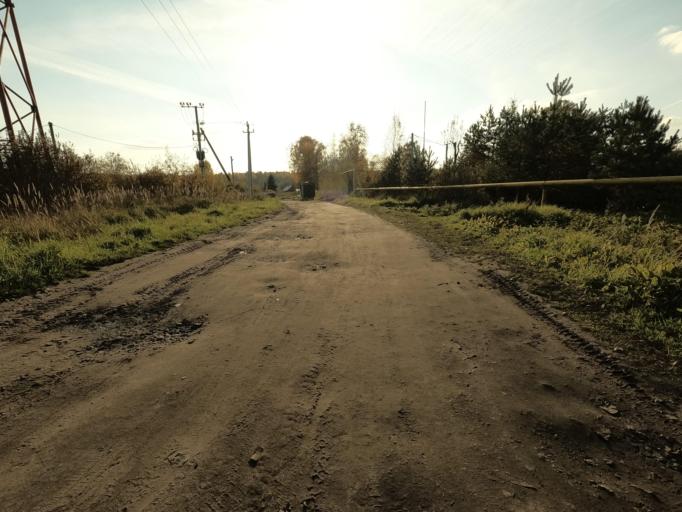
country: RU
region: Leningrad
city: Mga
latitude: 59.7459
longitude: 31.0609
